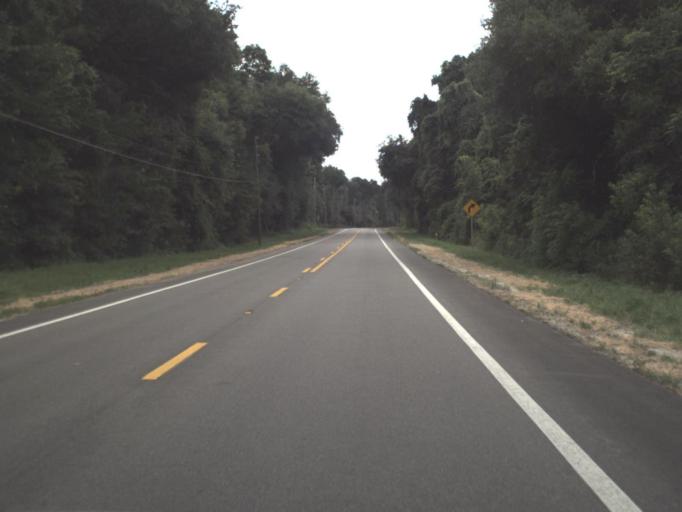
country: US
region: Florida
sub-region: Alachua County
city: Archer
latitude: 29.5096
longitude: -82.5037
